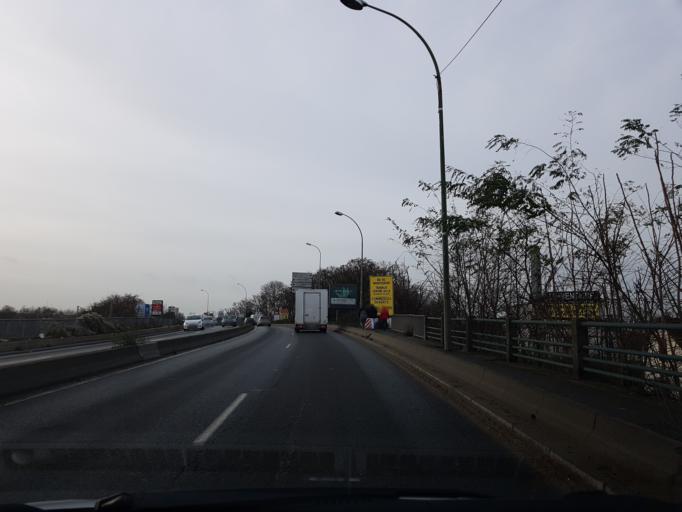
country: FR
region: Ile-de-France
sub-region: Departement du Val-de-Marne
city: Villeneuve-Saint-Georges
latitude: 48.7228
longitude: 2.4436
